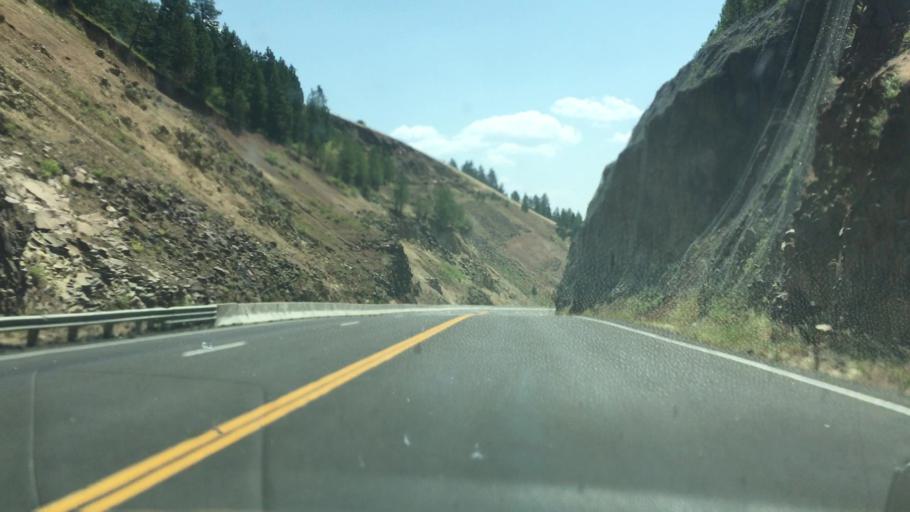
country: US
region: Idaho
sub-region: Idaho County
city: Grangeville
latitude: 45.8450
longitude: -116.2380
